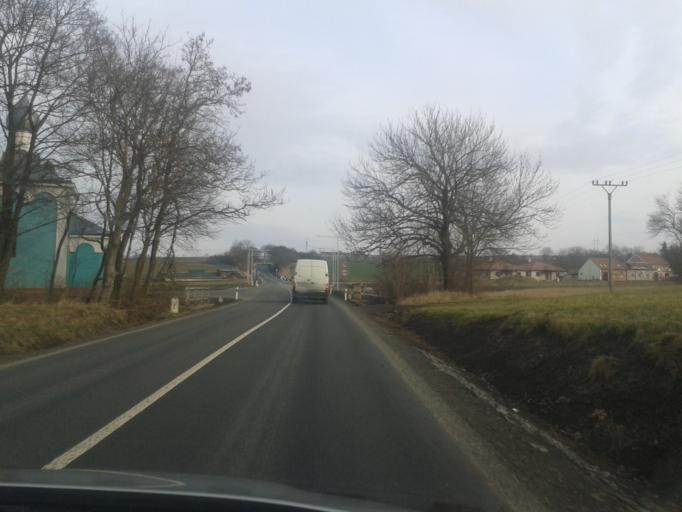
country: CZ
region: Olomoucky
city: Smrzice
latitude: 49.5148
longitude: 17.1038
